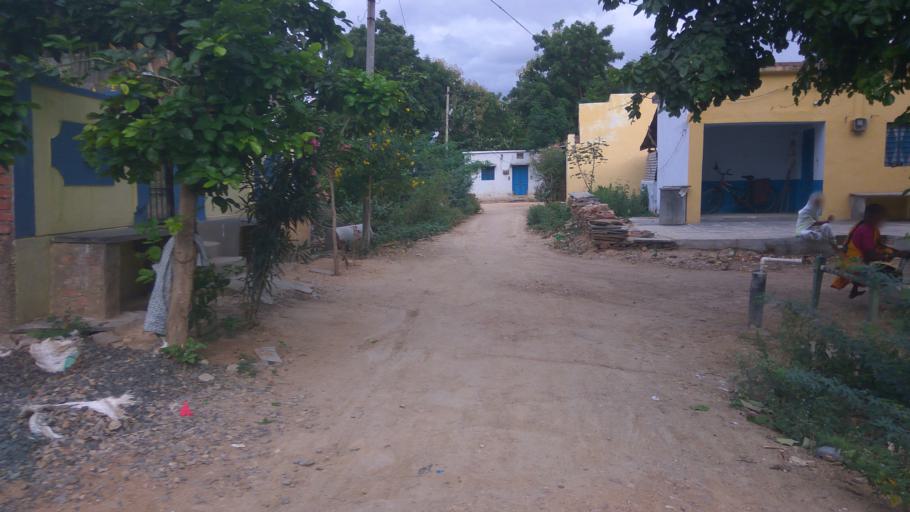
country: IN
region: Andhra Pradesh
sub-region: Prakasam
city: Cumbum
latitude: 15.5905
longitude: 79.1091
